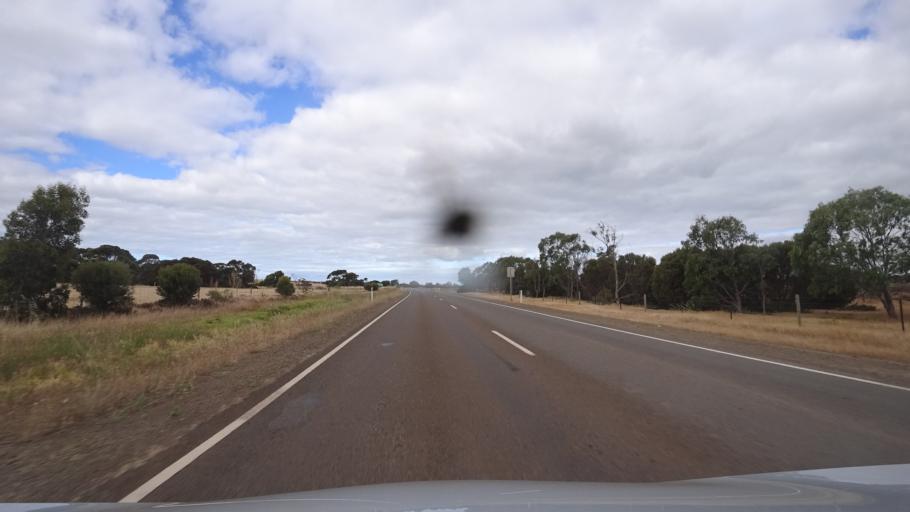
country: AU
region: South Australia
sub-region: Kangaroo Island
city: Kingscote
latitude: -35.6792
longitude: 137.5693
